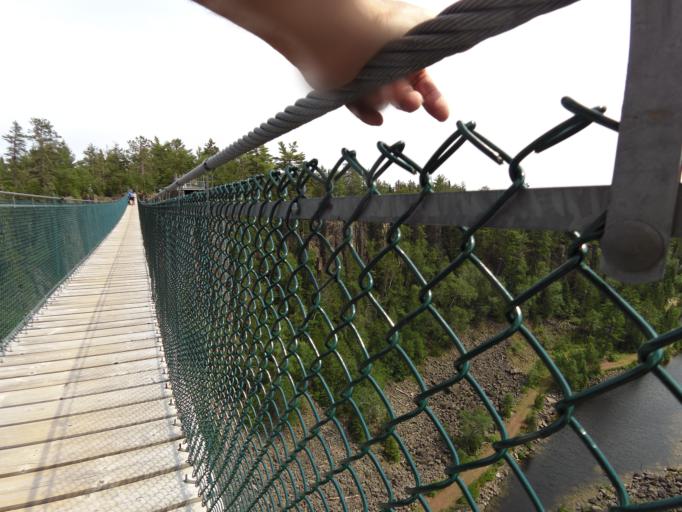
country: CA
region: Ontario
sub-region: Thunder Bay District
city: Thunder Bay
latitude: 48.8021
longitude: -88.6176
